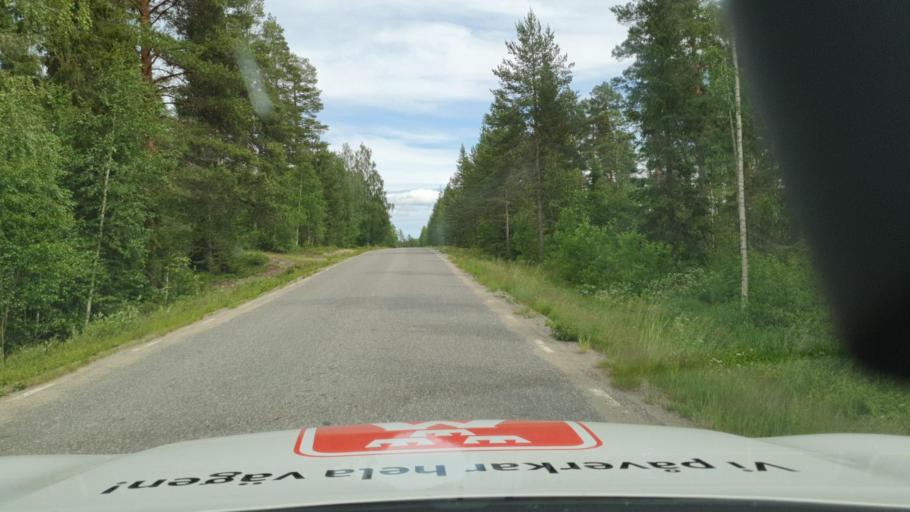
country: SE
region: Vaesterbotten
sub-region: Skelleftea Kommun
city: Viken
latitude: 64.4981
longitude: 20.8857
